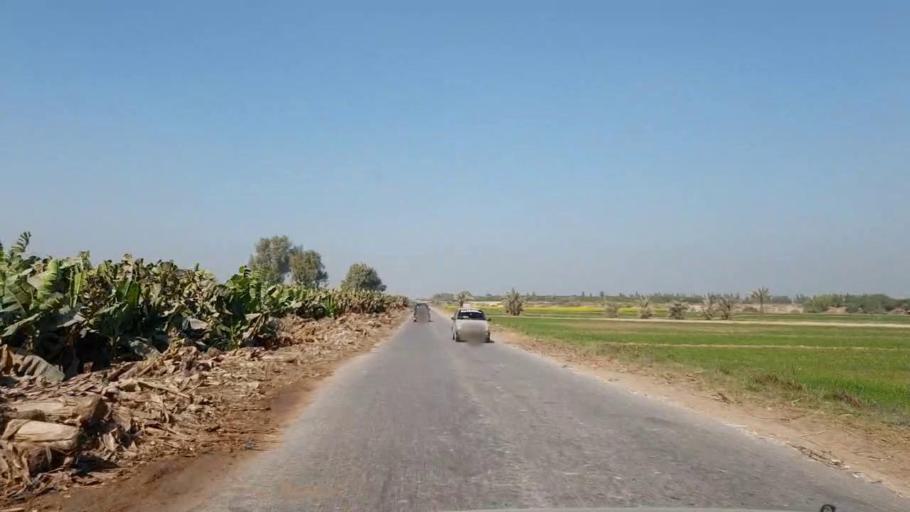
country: PK
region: Sindh
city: Tando Adam
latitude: 25.6466
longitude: 68.5920
